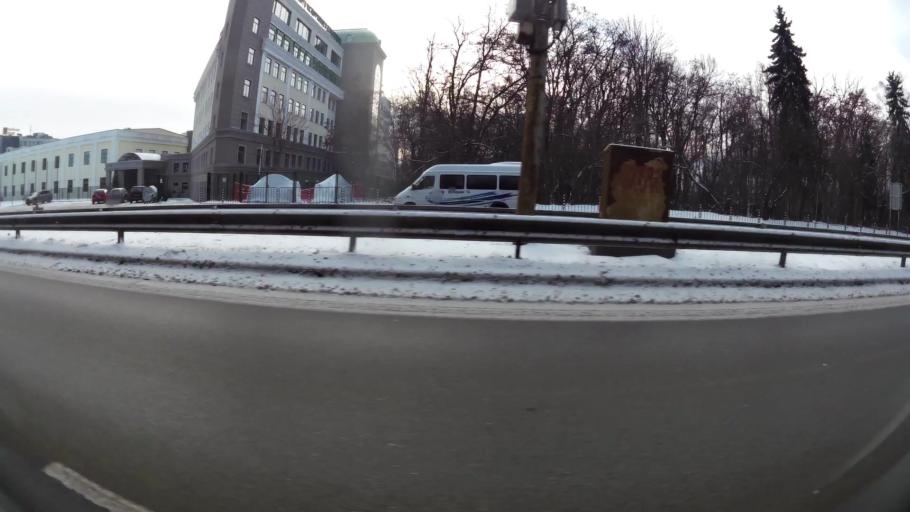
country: BG
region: Sofia-Capital
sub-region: Stolichna Obshtina
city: Sofia
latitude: 42.6666
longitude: 23.3226
